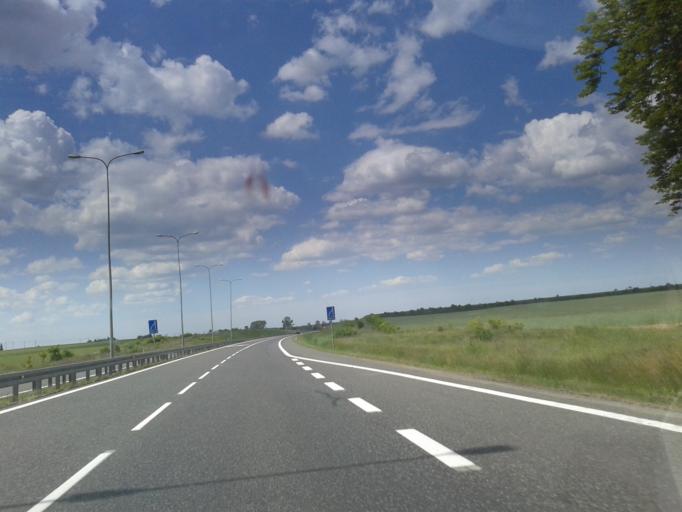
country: PL
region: Pomeranian Voivodeship
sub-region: Powiat chojnicki
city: Chojnice
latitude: 53.6789
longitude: 17.5813
